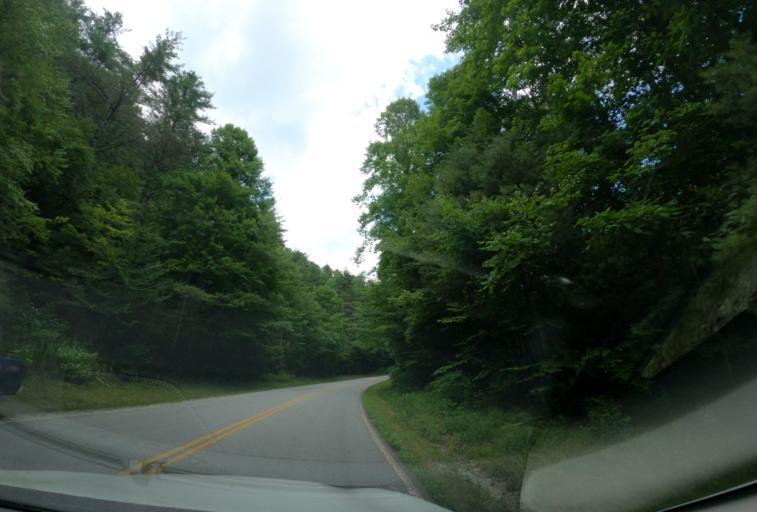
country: US
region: South Carolina
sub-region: Oconee County
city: Walhalla
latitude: 35.0384
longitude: -83.0220
